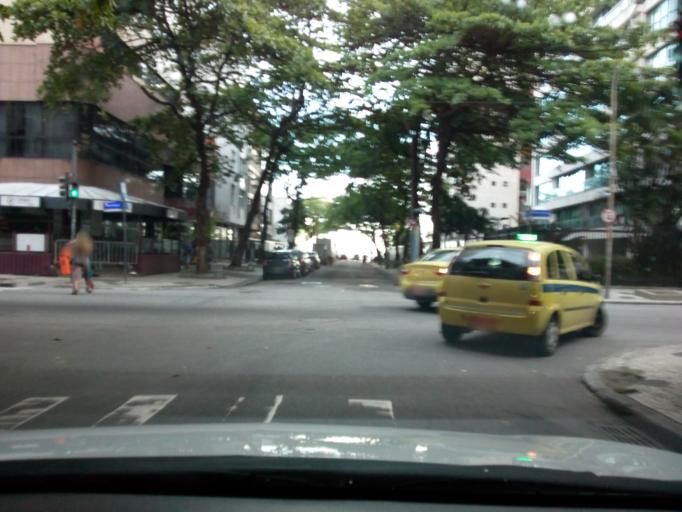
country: BR
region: Rio de Janeiro
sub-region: Rio De Janeiro
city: Rio de Janeiro
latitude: -22.9853
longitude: -43.2008
